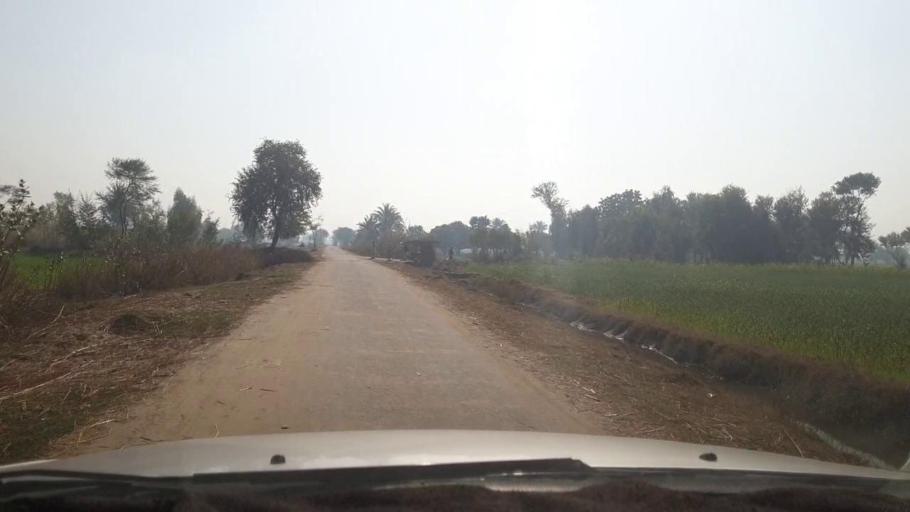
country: PK
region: Sindh
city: Khanpur
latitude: 27.7462
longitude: 69.5030
